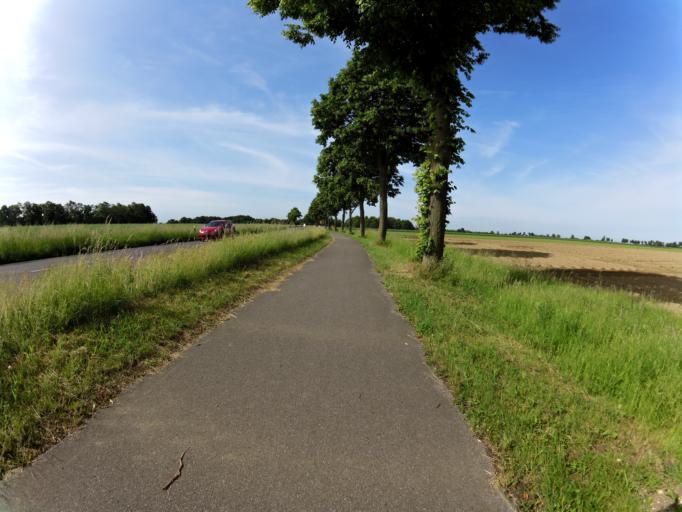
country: DE
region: North Rhine-Westphalia
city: Geilenkirchen
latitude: 50.9615
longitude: 6.1059
